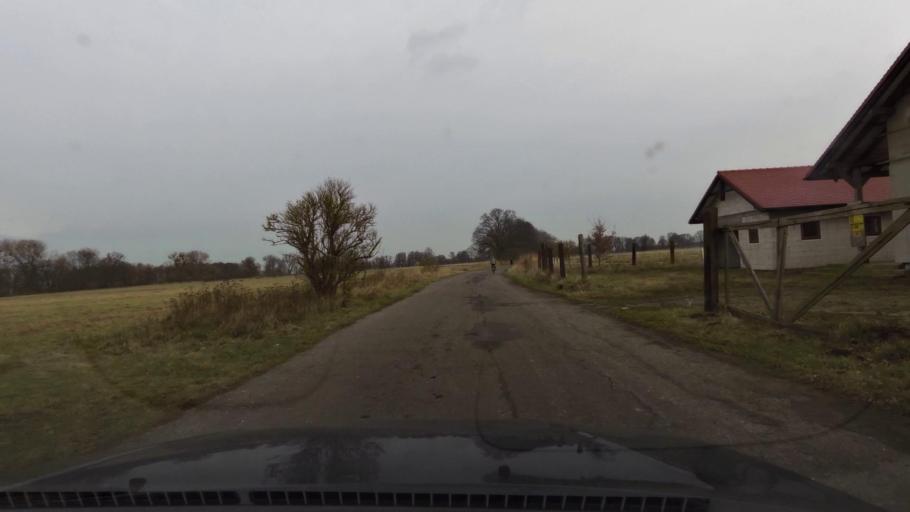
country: PL
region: West Pomeranian Voivodeship
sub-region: Powiat goleniowski
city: Stepnica
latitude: 53.7238
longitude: 14.5546
